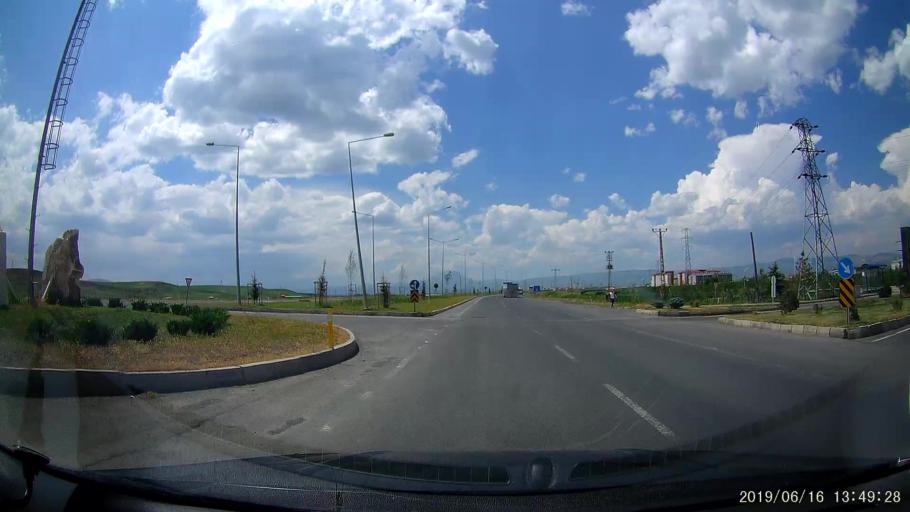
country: TR
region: Agri
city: Agri
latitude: 39.7176
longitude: 42.9903
